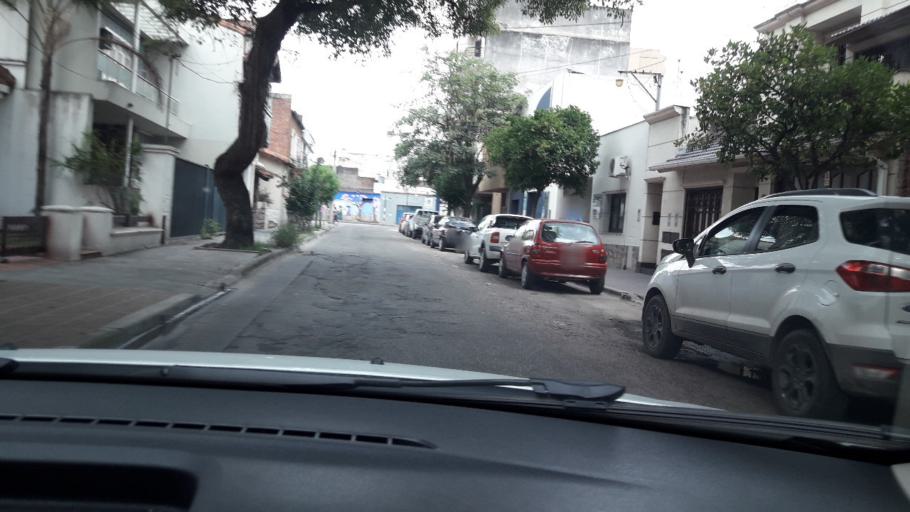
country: AR
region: Jujuy
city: San Salvador de Jujuy
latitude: -24.1853
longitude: -65.3124
